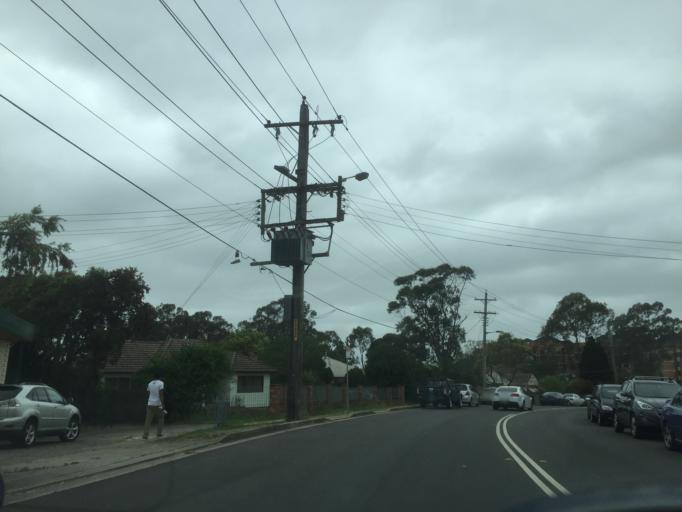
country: AU
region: New South Wales
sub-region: Blacktown
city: Blacktown
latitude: -33.7688
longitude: 150.9012
